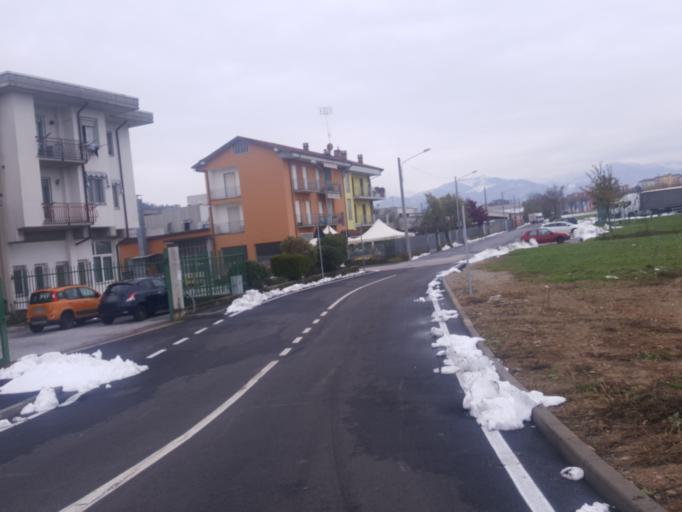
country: IT
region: Piedmont
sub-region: Provincia di Cuneo
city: Breo
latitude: 44.4026
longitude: 7.8243
